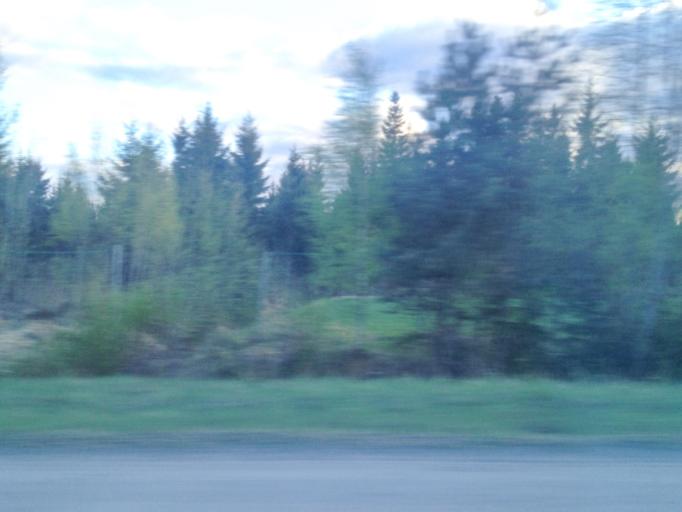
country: FI
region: Haeme
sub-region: Haemeenlinna
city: Kalvola
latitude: 61.0881
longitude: 24.1933
